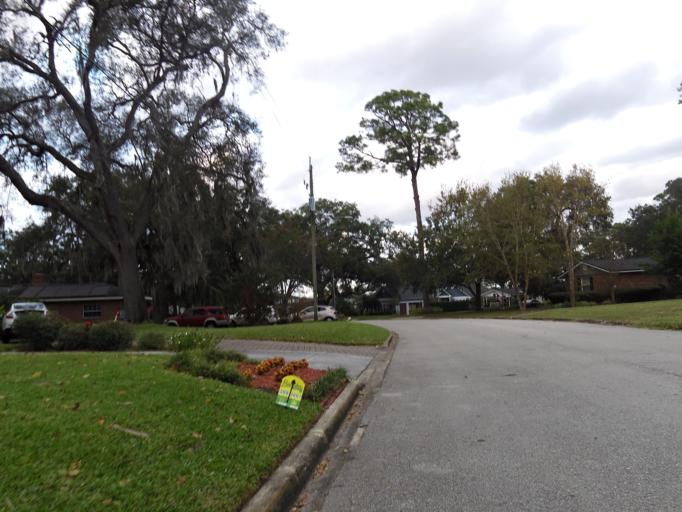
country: US
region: Florida
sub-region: Duval County
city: Jacksonville
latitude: 30.3102
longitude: -81.6358
